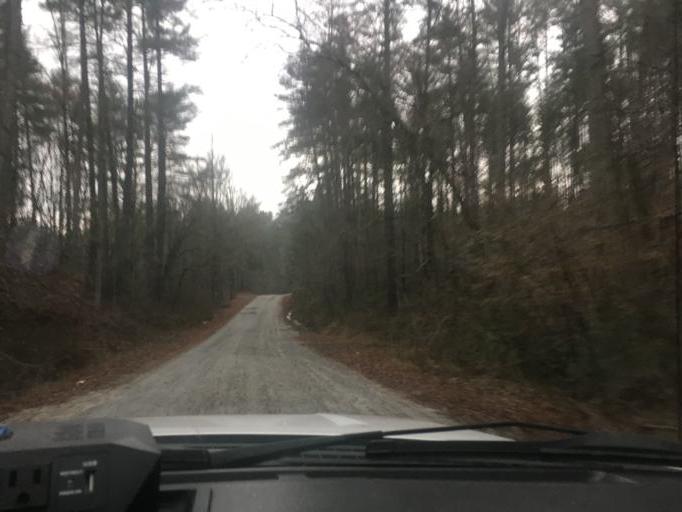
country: US
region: Georgia
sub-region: Dawson County
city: Dawsonville
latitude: 34.4422
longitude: -84.2086
